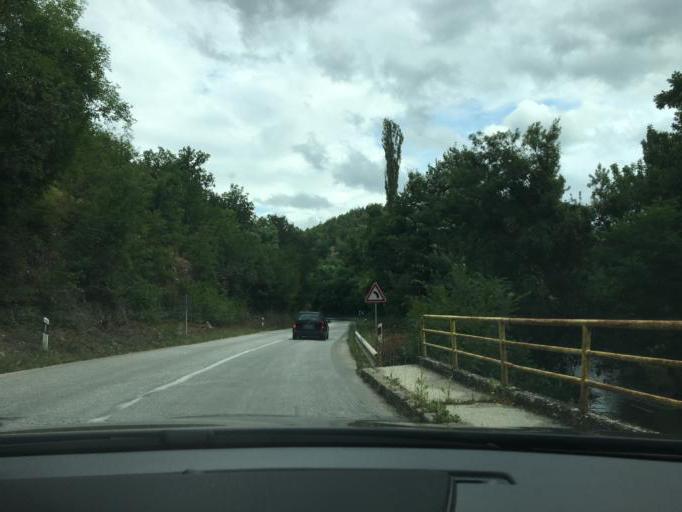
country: MK
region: Kratovo
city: Kratovo
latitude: 42.1732
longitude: 22.2239
